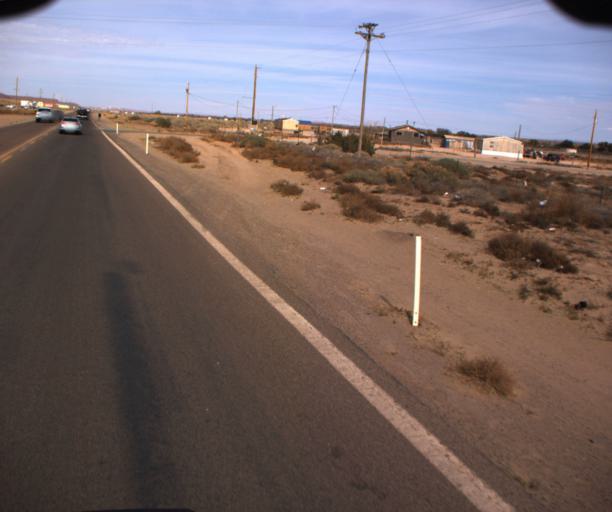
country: US
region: Arizona
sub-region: Apache County
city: Chinle
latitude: 36.1671
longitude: -109.5856
